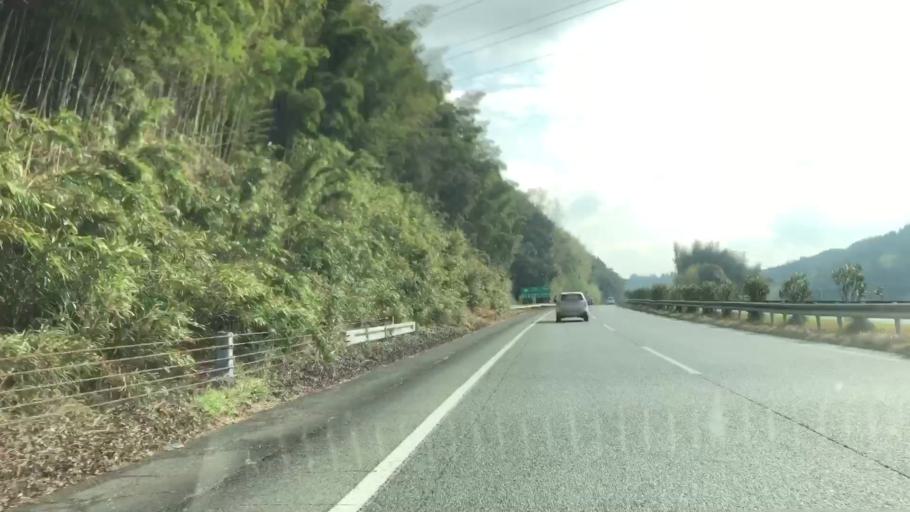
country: JP
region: Kumamoto
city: Yamaga
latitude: 33.0385
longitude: 130.5706
